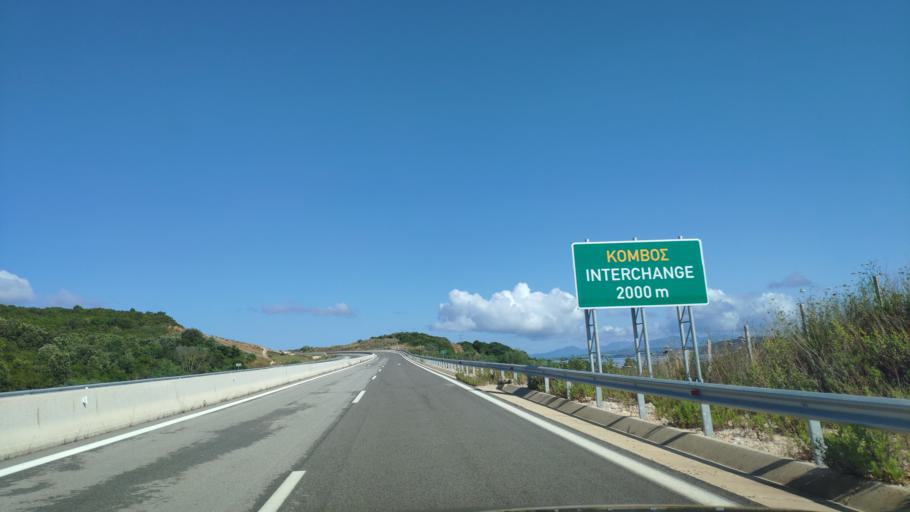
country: GR
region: West Greece
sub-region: Nomos Aitolias kai Akarnanias
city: Vonitsa
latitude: 38.9128
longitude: 20.8284
